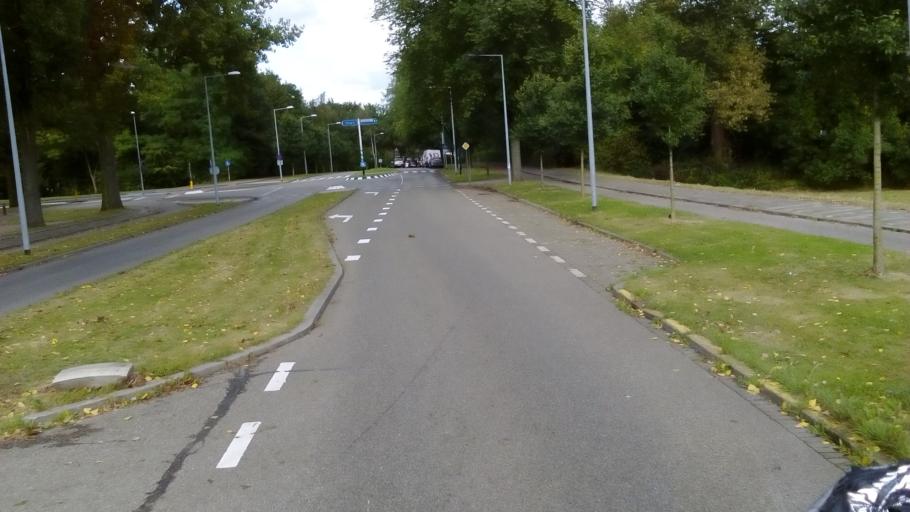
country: NL
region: South Holland
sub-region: Gemeente Schiedam
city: Schiedam
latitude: 51.9059
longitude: 4.3971
